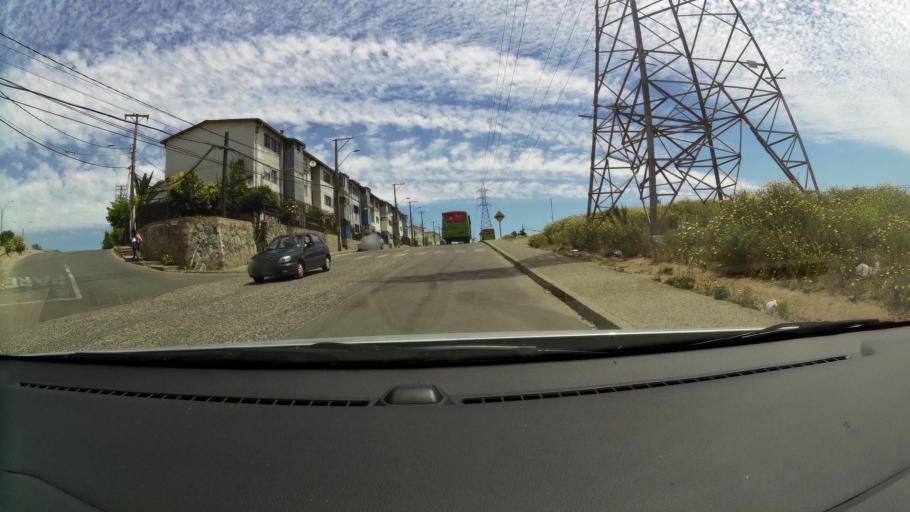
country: CL
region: Valparaiso
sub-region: Provincia de Valparaiso
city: Vina del Mar
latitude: -33.0569
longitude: -71.5591
